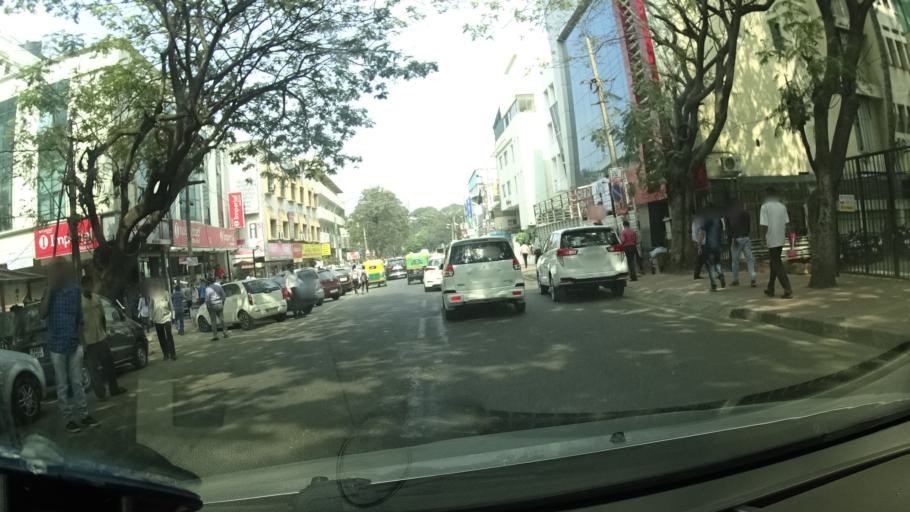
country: IN
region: Karnataka
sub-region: Bangalore Urban
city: Bangalore
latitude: 12.9908
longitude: 77.5936
